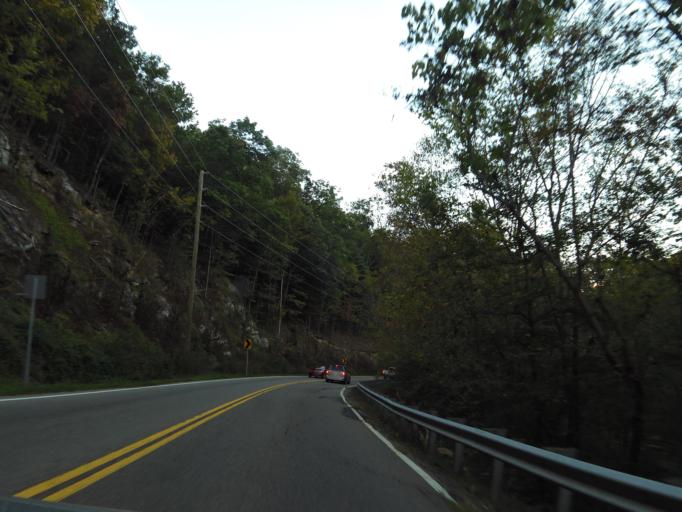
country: US
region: Tennessee
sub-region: Sevier County
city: Pigeon Forge
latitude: 35.7559
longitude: -83.6258
